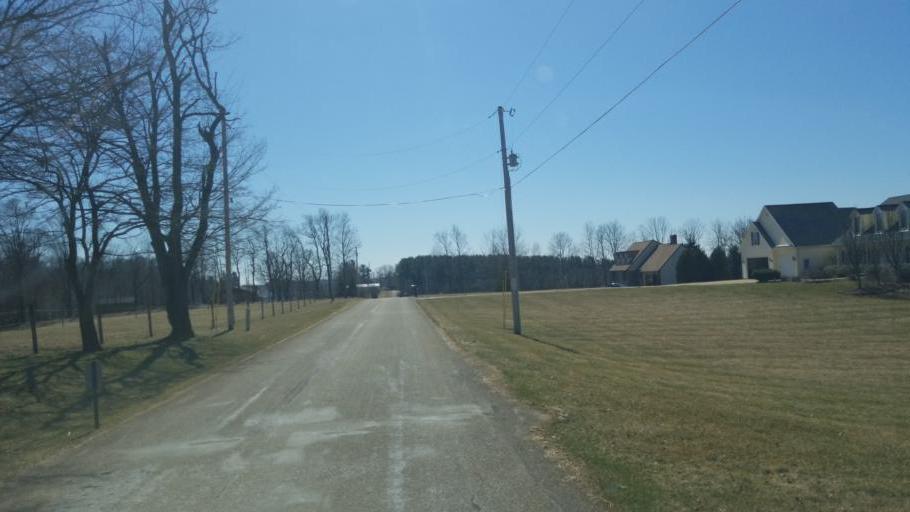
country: US
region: Ohio
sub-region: Richland County
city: Lexington
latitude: 40.6496
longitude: -82.6019
